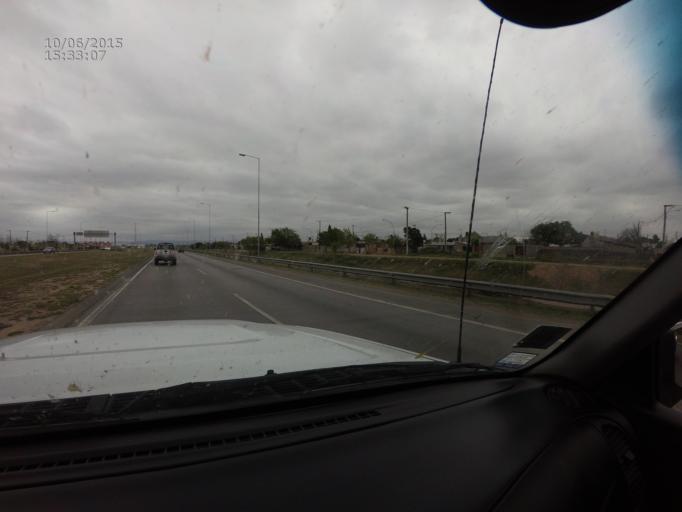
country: AR
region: Cordoba
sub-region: Departamento de Capital
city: Cordoba
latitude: -31.3610
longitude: -64.1559
